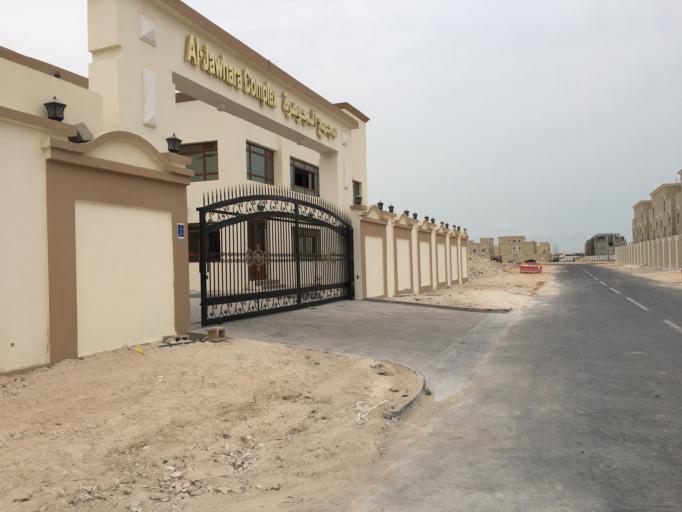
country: QA
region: Baladiyat Umm Salal
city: Umm Salal Muhammad
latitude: 25.3918
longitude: 51.4374
